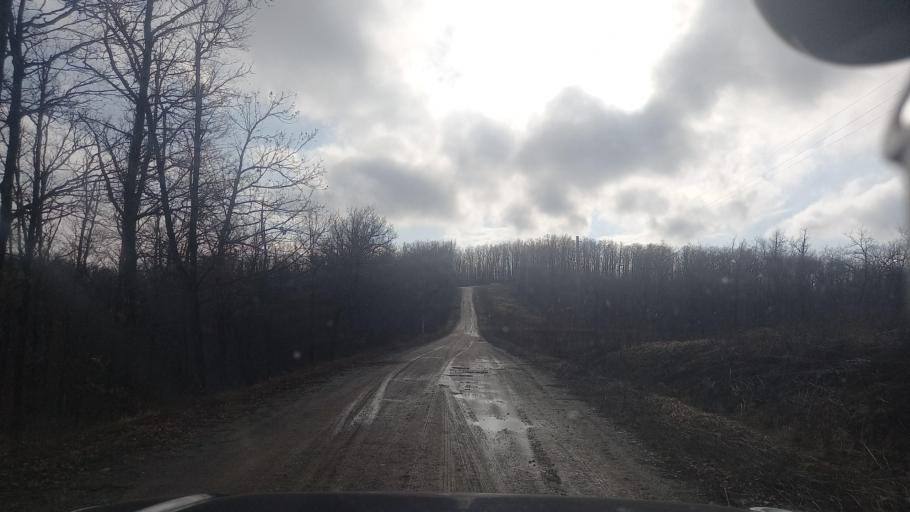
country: RU
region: Krasnodarskiy
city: Smolenskaya
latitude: 44.7439
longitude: 38.7768
